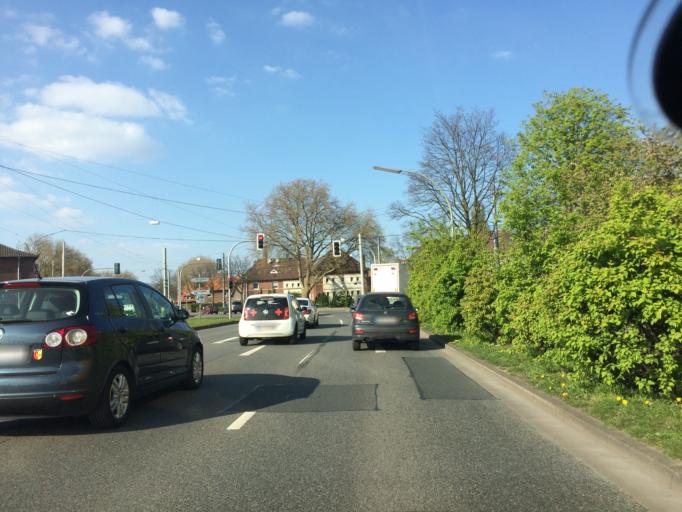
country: DE
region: North Rhine-Westphalia
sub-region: Regierungsbezirk Munster
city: Gelsenkirchen
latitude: 51.4828
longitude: 7.1301
